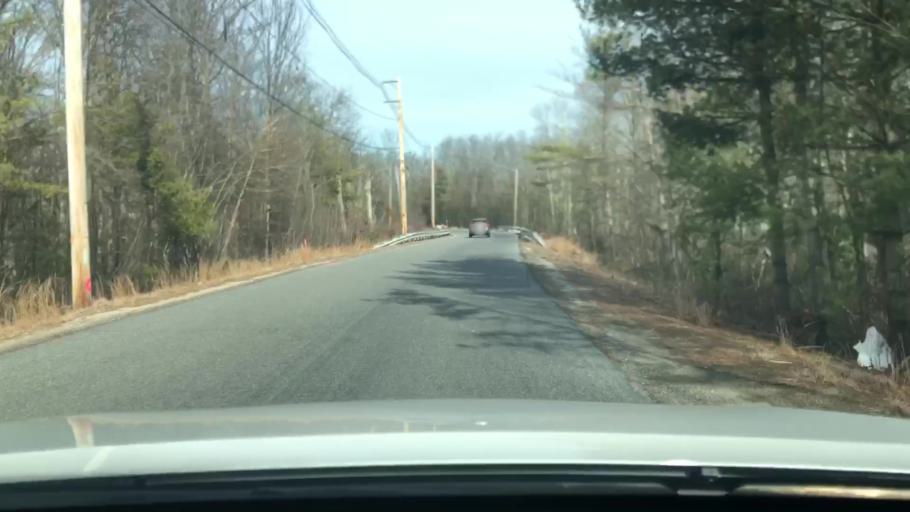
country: US
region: Massachusetts
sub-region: Worcester County
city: Milford
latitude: 42.1444
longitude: -71.4873
